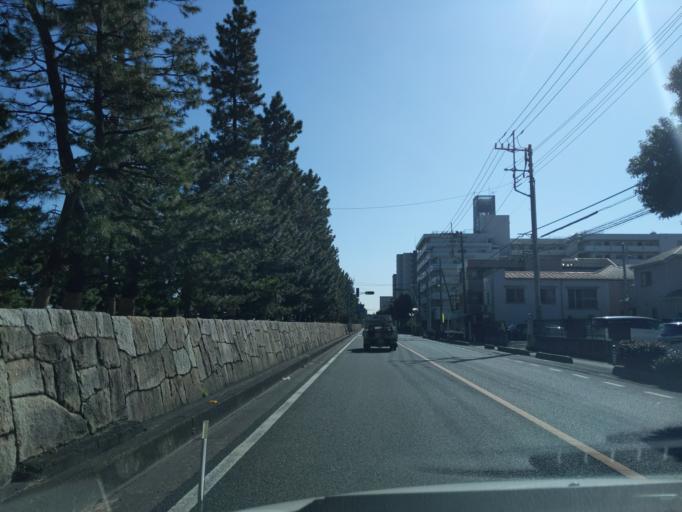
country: JP
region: Saitama
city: Soka
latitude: 35.8418
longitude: 139.8048
